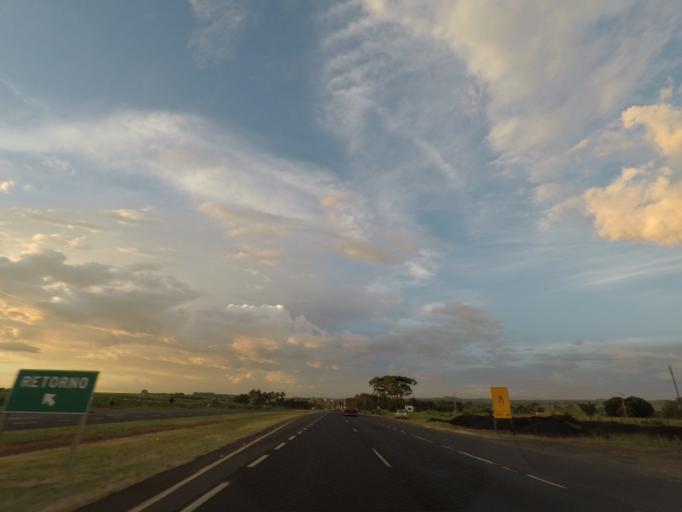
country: BR
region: Minas Gerais
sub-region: Uberaba
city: Uberaba
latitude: -19.6632
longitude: -48.0011
